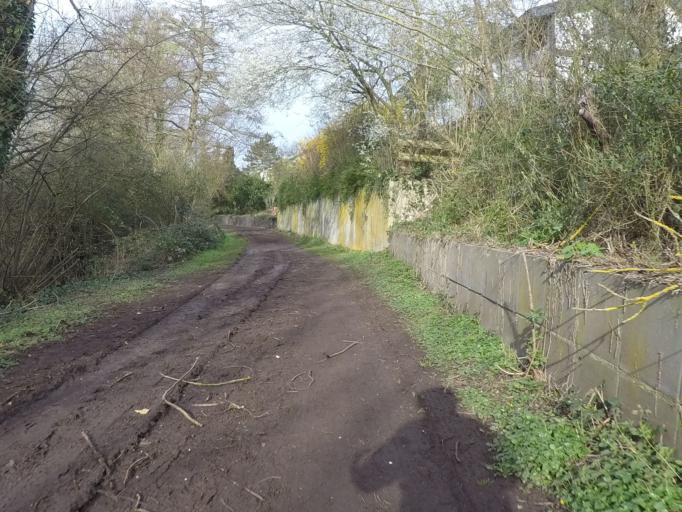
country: DE
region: Rheinland-Pfalz
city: Billigheim-Ingenheim
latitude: 49.1379
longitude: 8.0922
